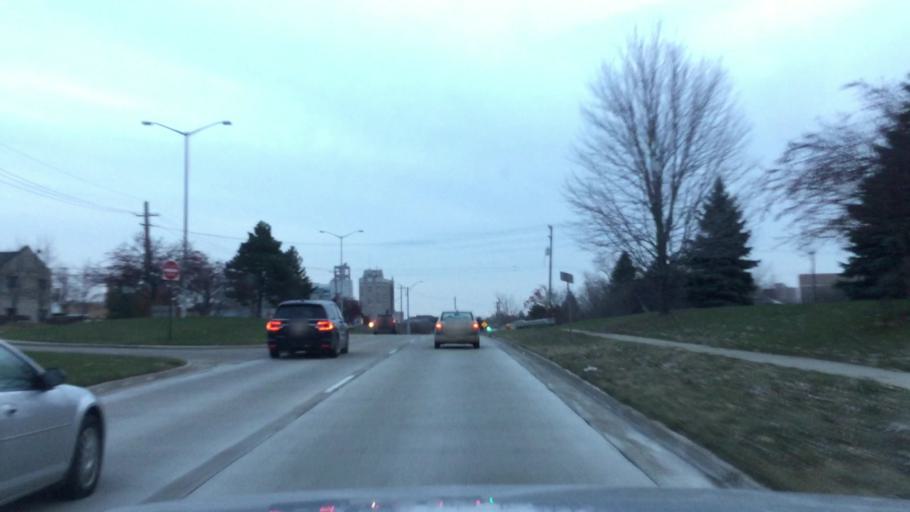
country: US
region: Michigan
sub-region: Oakland County
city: Pontiac
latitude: 42.6330
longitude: -83.3004
